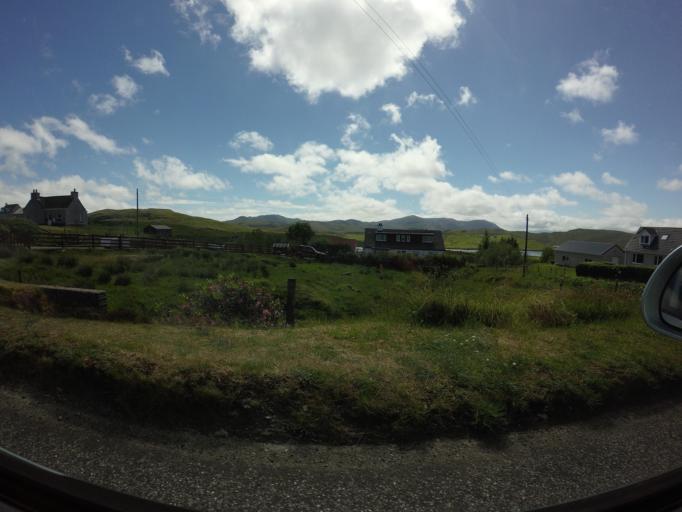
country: GB
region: Scotland
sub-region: Eilean Siar
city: Stornoway
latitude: 58.0914
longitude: -6.6094
